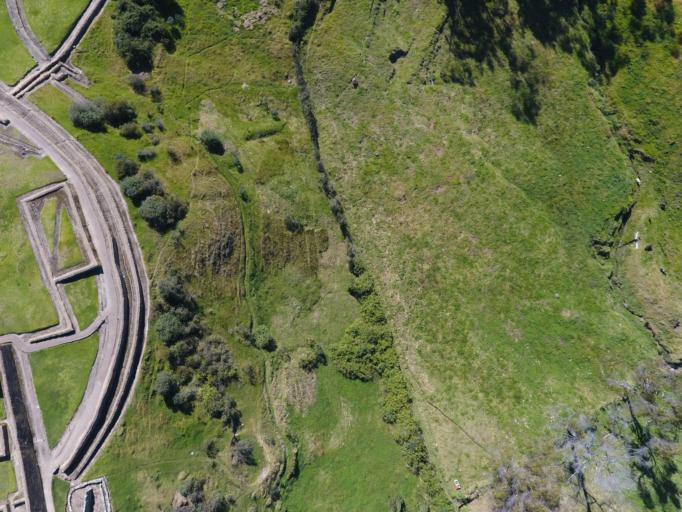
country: EC
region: Canar
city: Canar
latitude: -2.5405
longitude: -78.8751
